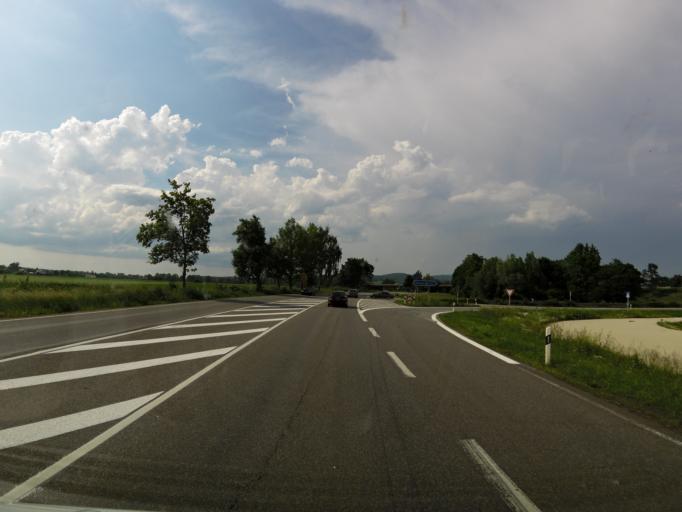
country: DE
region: Bavaria
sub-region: Lower Bavaria
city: Hengersberg
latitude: 48.7678
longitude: 13.0418
